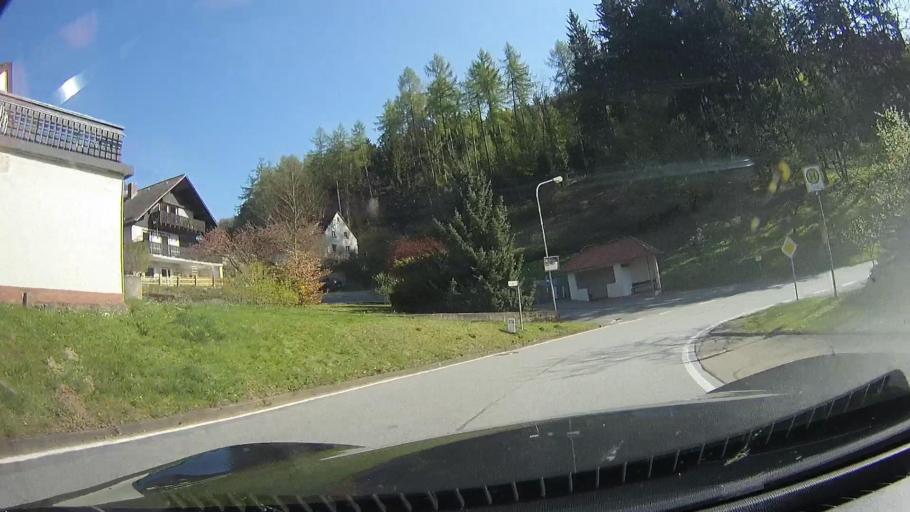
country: DE
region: Hesse
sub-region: Regierungsbezirk Darmstadt
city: Rothenberg
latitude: 49.4798
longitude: 8.9216
